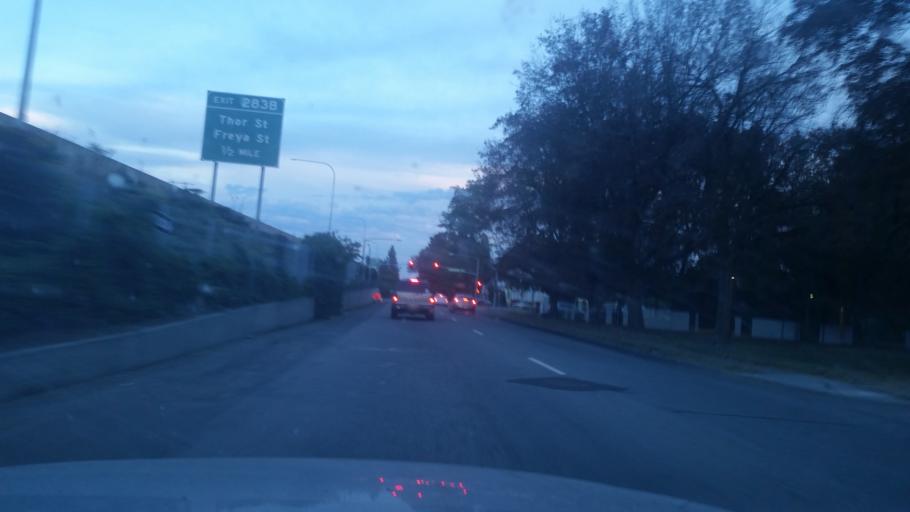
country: US
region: Washington
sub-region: Spokane County
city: Spokane
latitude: 47.6537
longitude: -117.3769
